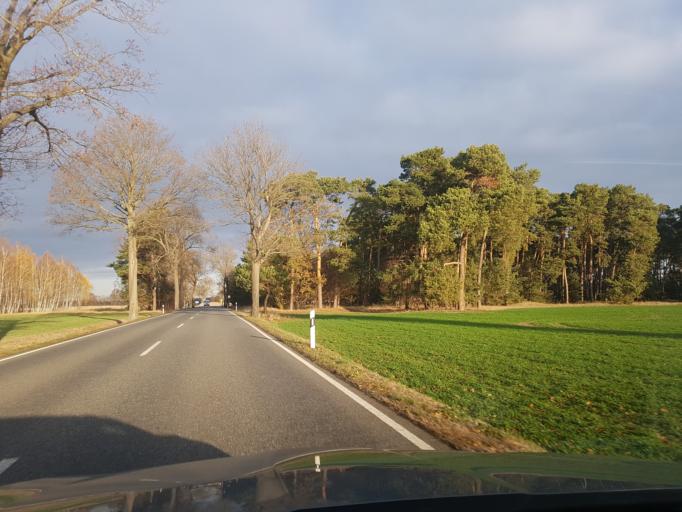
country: DE
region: Brandenburg
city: Kasel-Golzig
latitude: 51.9318
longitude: 13.6641
